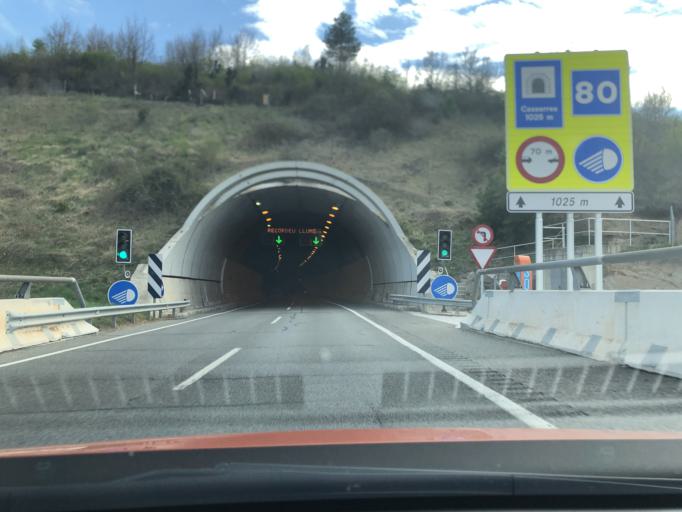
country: ES
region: Catalonia
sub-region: Provincia de Barcelona
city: Gironella
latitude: 42.0041
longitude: 1.8810
